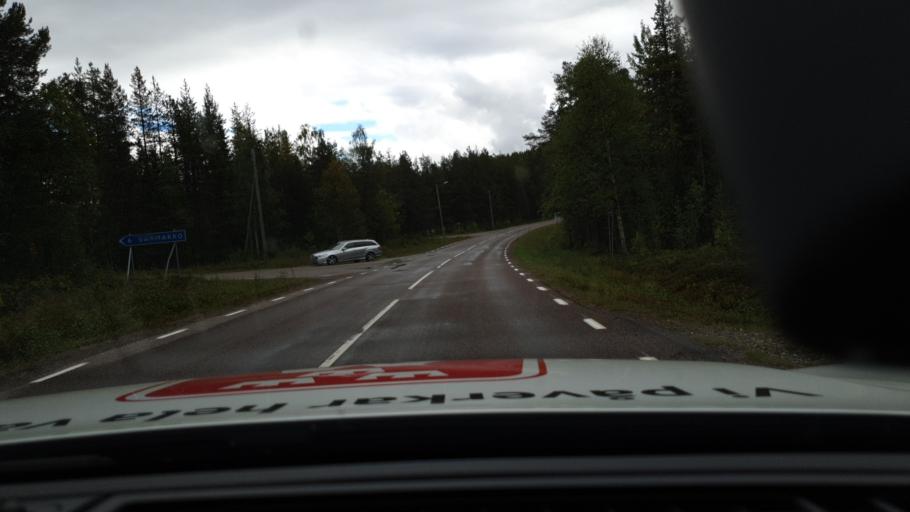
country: SE
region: Norrbotten
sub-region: Gallivare Kommun
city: Gaellivare
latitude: 66.9256
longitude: 21.5379
